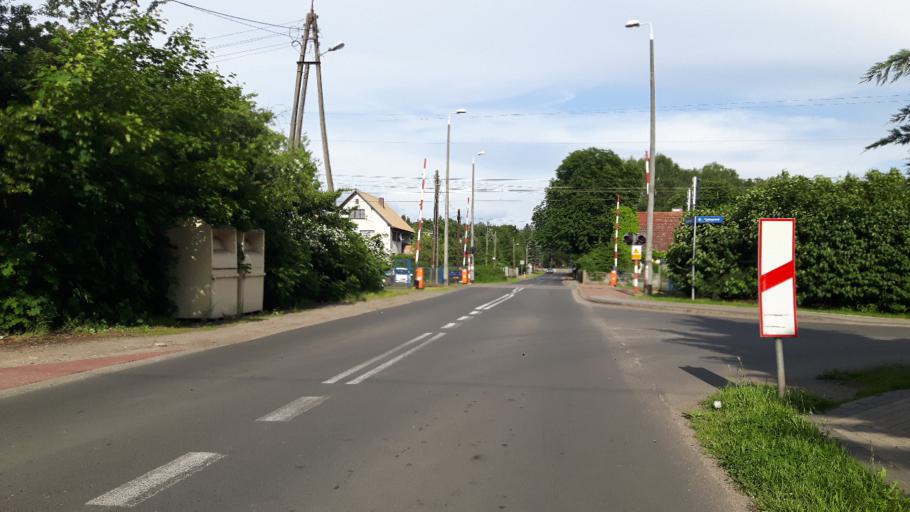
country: PL
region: West Pomeranian Voivodeship
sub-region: Powiat goleniowski
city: Goleniow
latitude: 53.4617
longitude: 14.7837
